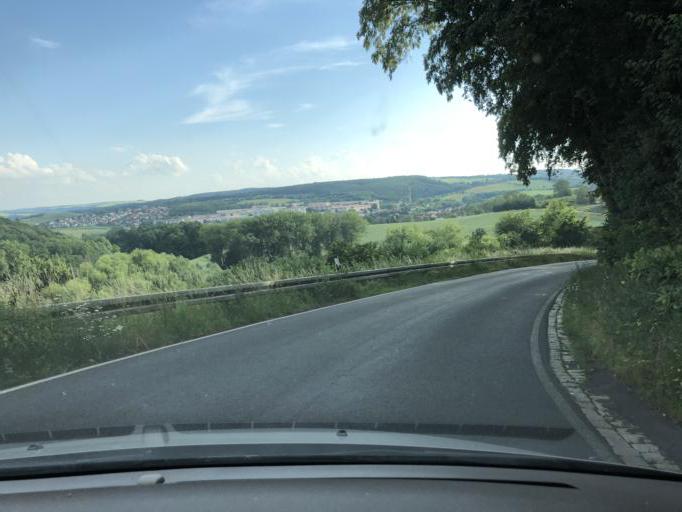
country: DE
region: Saxony
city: Freital
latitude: 51.0261
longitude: 13.6499
